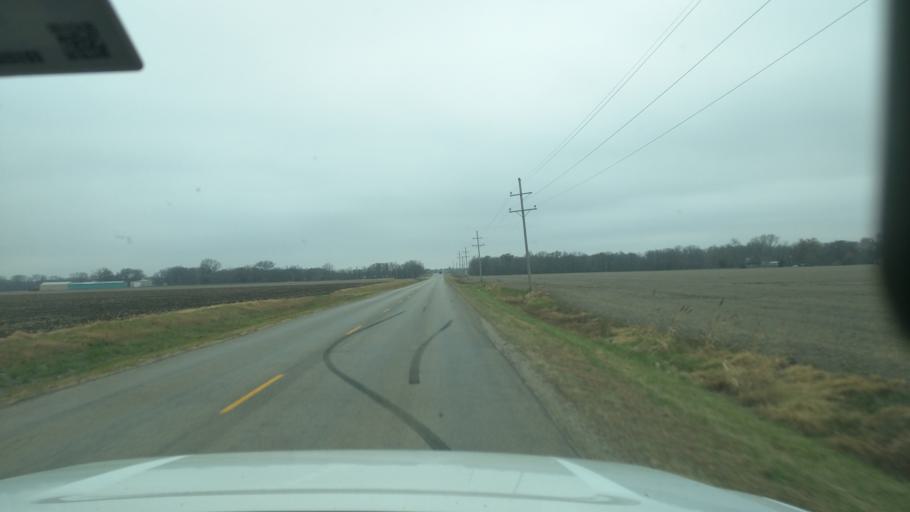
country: US
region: Kansas
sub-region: Lyon County
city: Emporia
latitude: 38.4773
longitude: -96.2530
